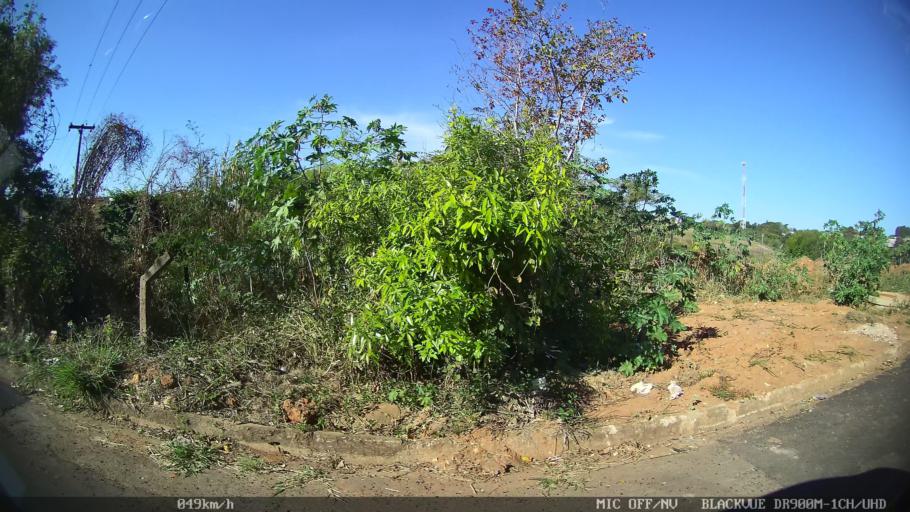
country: BR
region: Sao Paulo
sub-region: Franca
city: Franca
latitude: -20.4939
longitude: -47.4136
